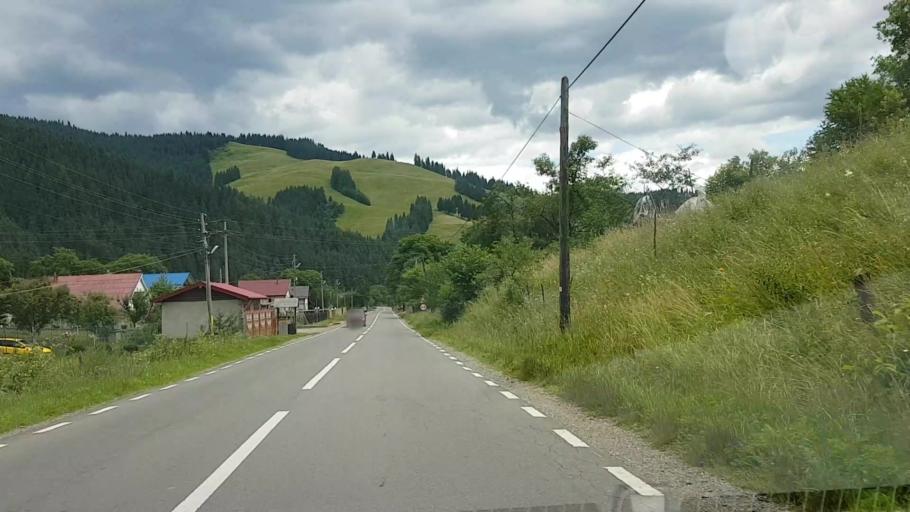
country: RO
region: Neamt
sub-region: Comuna Farcasa
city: Farcasa
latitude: 47.1356
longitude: 25.8872
